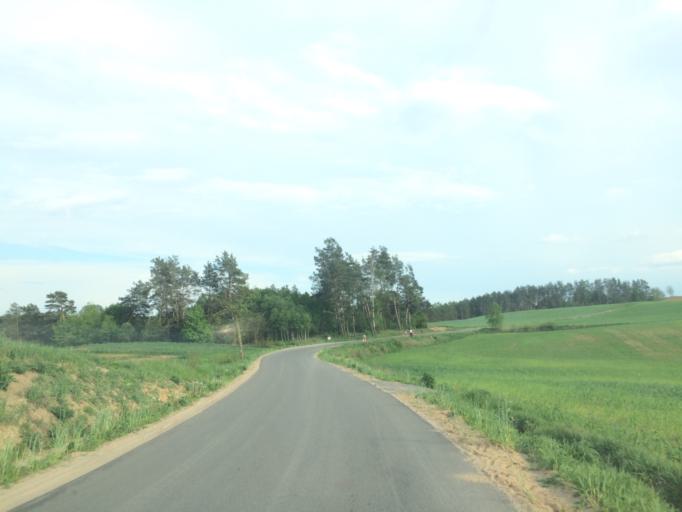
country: PL
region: Kujawsko-Pomorskie
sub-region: Powiat brodnicki
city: Brzozie
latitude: 53.3707
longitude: 19.7096
